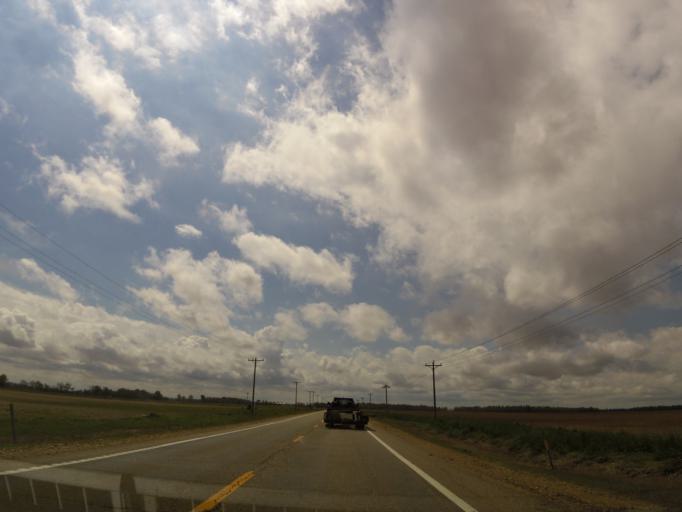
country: US
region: Arkansas
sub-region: Clay County
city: Corning
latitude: 36.3526
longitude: -90.5251
